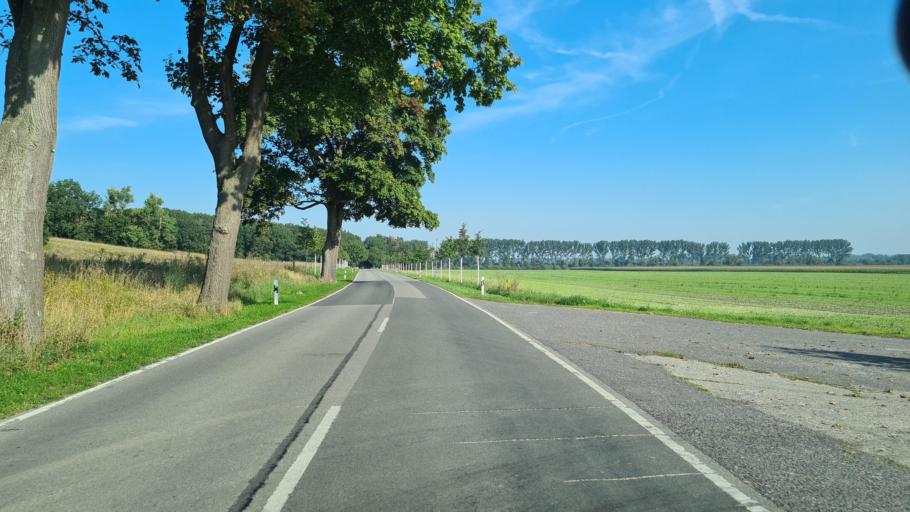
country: DE
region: Brandenburg
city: Pessin
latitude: 52.6970
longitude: 12.6490
